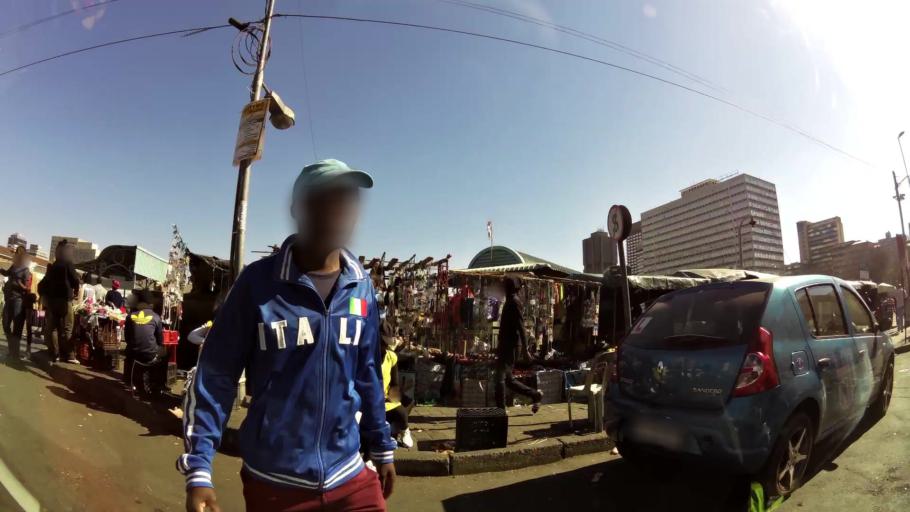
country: ZA
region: Gauteng
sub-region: City of Johannesburg Metropolitan Municipality
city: Johannesburg
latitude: -26.1971
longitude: 28.0446
